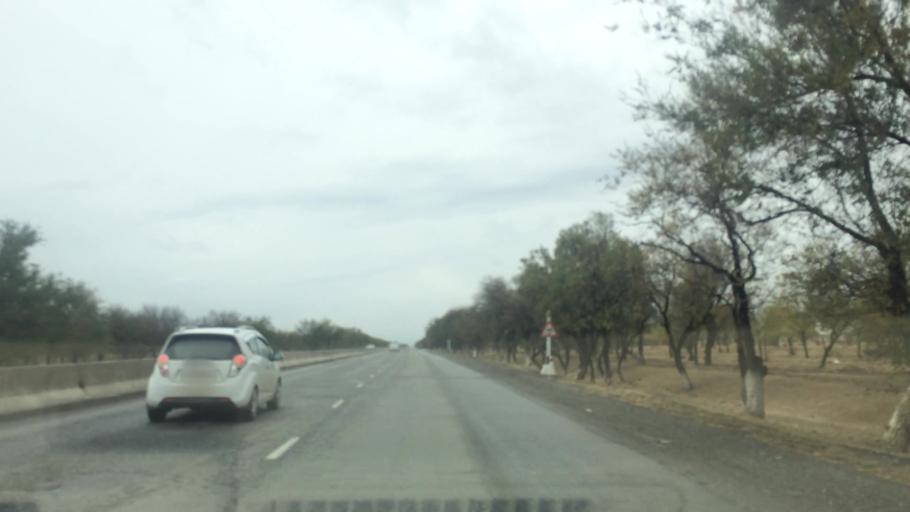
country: UZ
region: Samarqand
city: Bulung'ur
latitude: 39.8324
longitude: 67.4164
